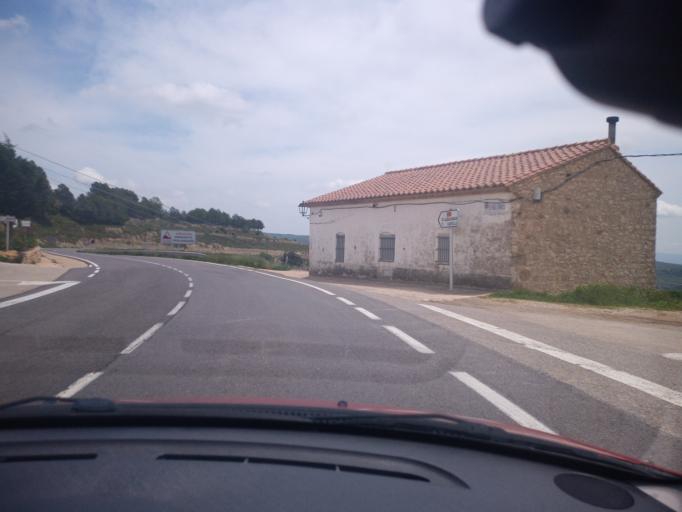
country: ES
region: Valencia
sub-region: Provincia de Castello
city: Ares del Maestre
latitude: 40.4541
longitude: -0.1421
